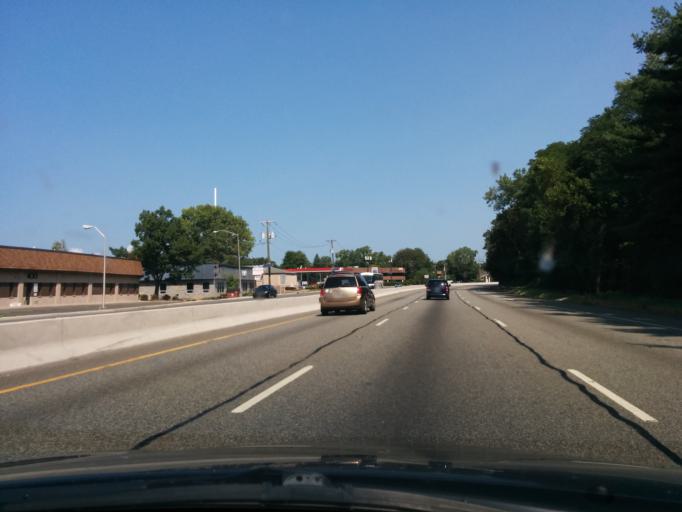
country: US
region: New Jersey
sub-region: Bergen County
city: Ho-Ho-Kus
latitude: 40.9881
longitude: -74.0936
